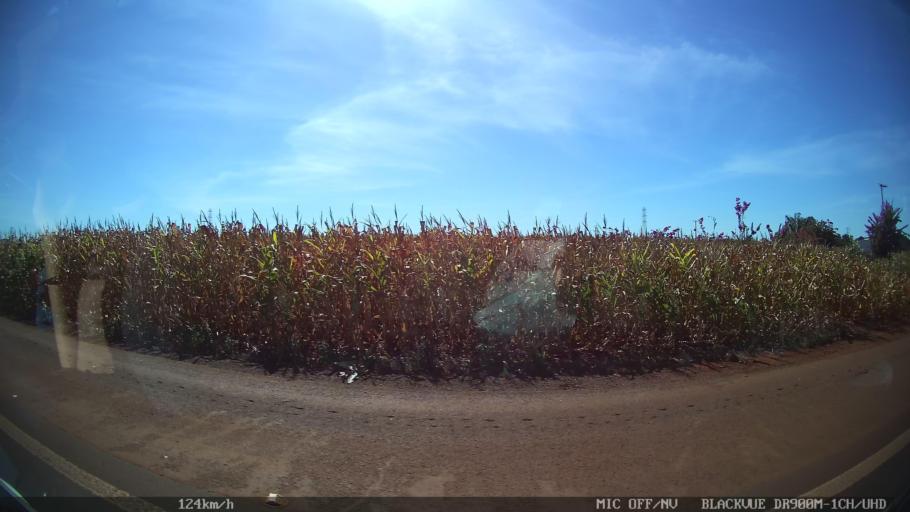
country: BR
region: Sao Paulo
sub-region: Guaira
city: Guaira
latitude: -20.4443
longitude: -48.3644
